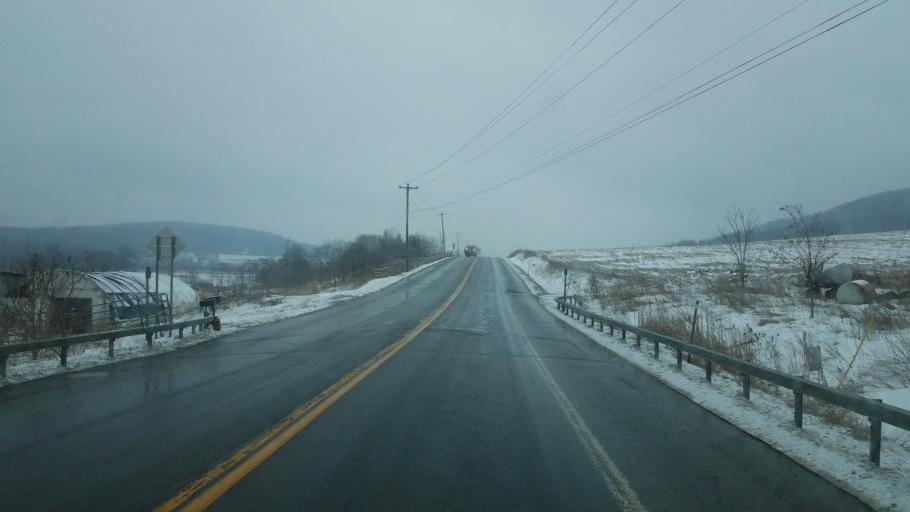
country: US
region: New York
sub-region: Steuben County
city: Canisteo
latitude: 42.1130
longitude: -77.4905
